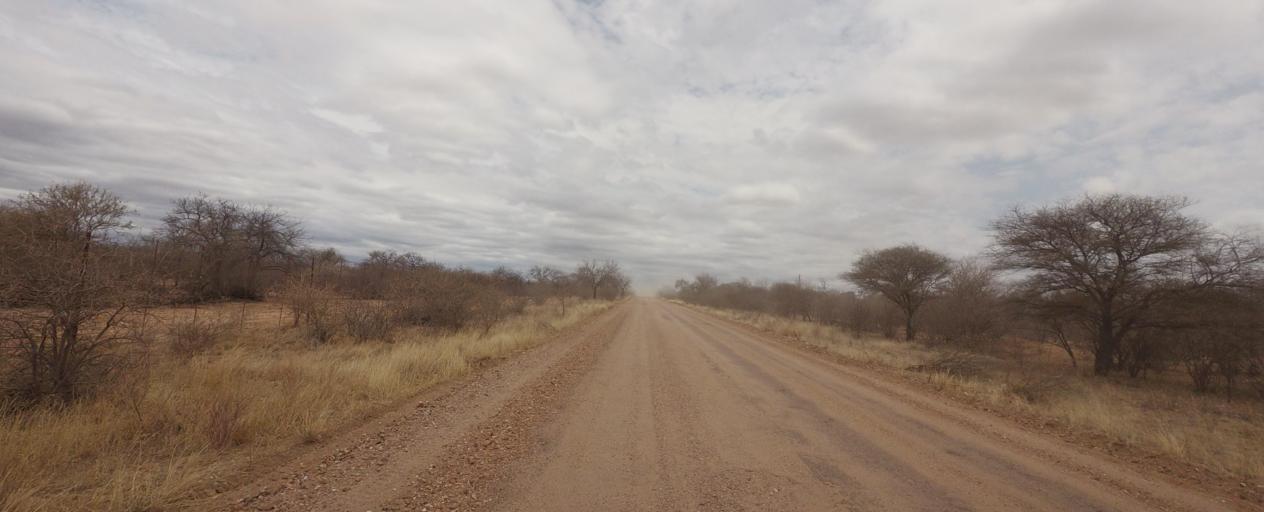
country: BW
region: Central
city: Mathathane
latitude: -22.6766
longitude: 28.6695
